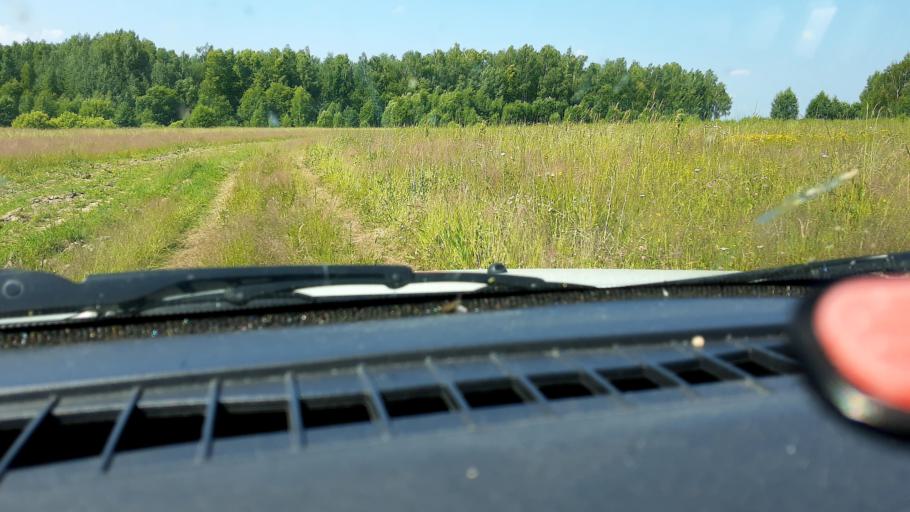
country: RU
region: Nizjnij Novgorod
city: Sharanga
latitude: 57.0457
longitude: 46.7255
